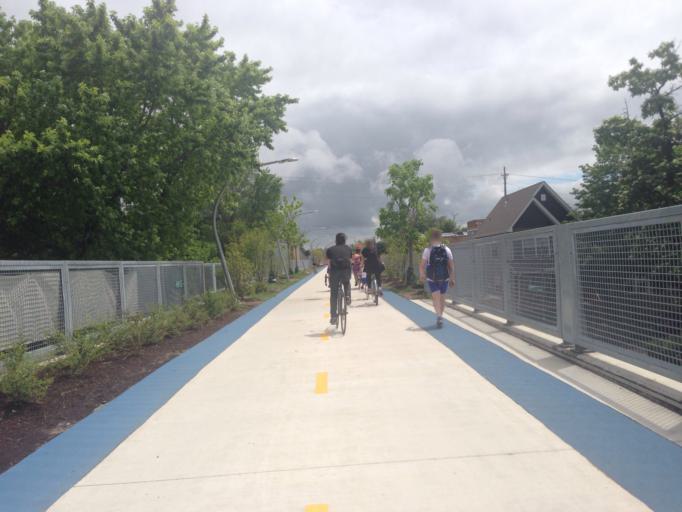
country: US
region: Illinois
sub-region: Cook County
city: Chicago
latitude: 41.9138
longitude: -87.7039
